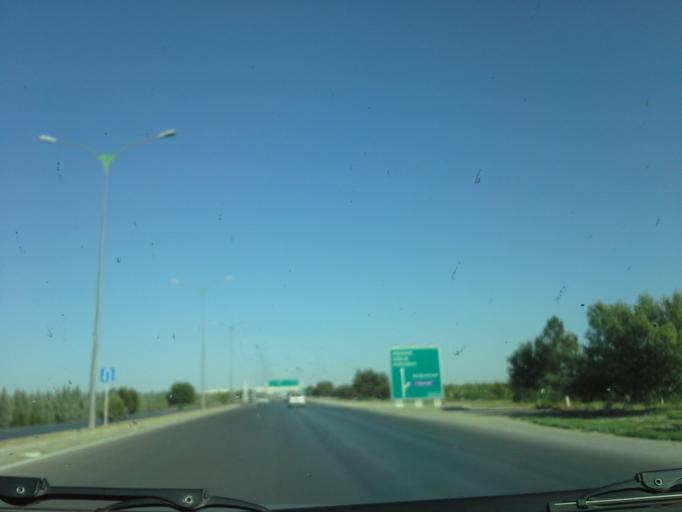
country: TM
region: Ahal
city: Abadan
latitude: 38.0917
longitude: 58.1028
